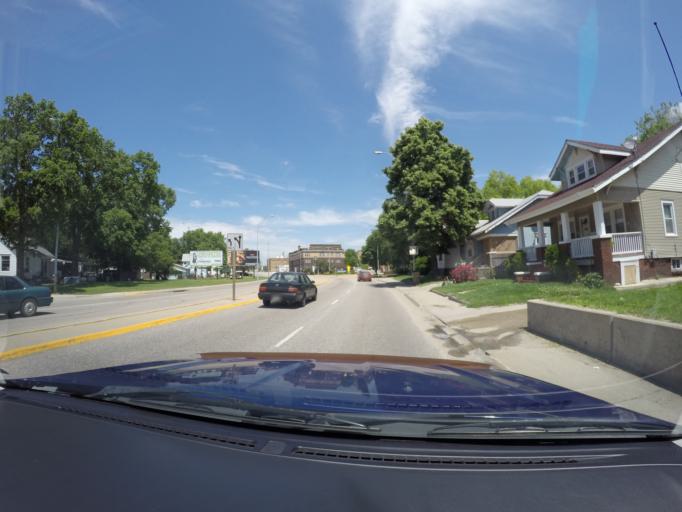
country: US
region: Nebraska
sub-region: Hall County
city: Grand Island
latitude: 40.9191
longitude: -98.3398
